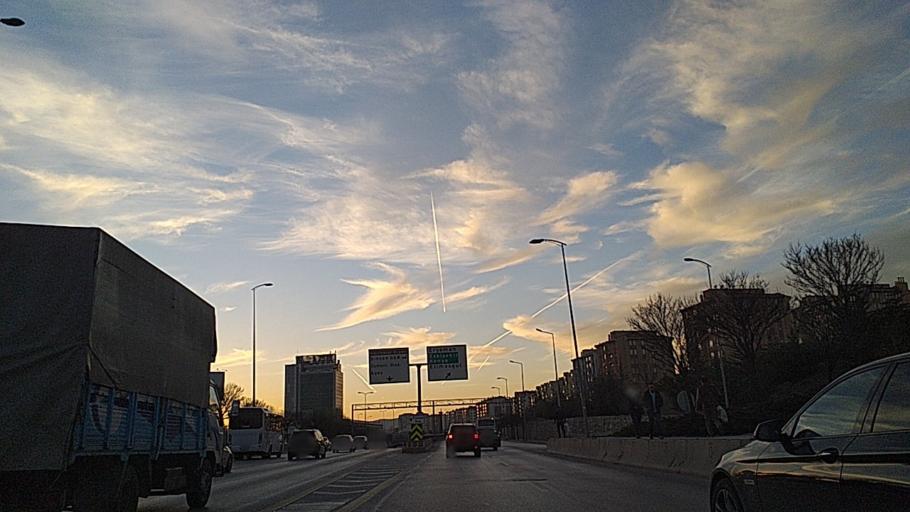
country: TR
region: Ankara
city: Etimesgut
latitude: 39.9672
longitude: 32.6293
